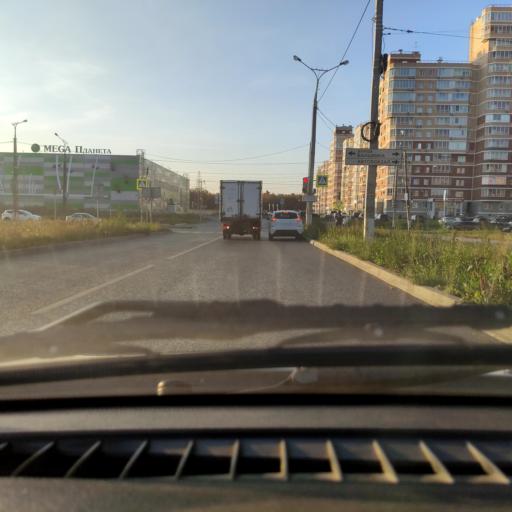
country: RU
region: Samara
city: Tol'yatti
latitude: 53.5015
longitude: 49.4212
